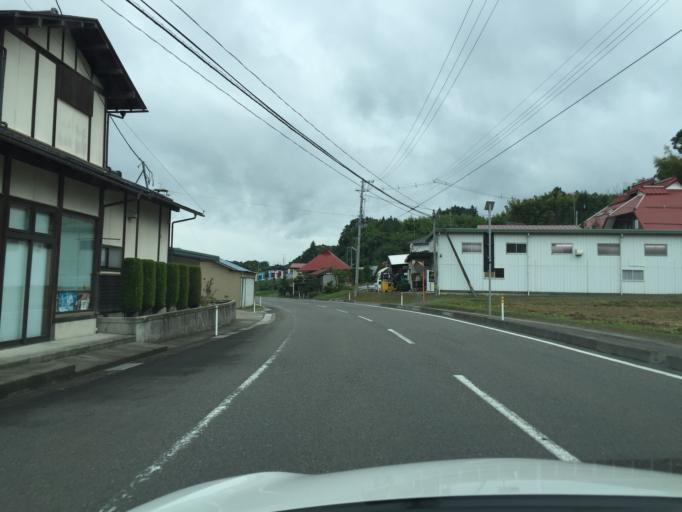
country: JP
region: Fukushima
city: Funehikimachi-funehiki
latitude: 37.4597
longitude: 140.5322
